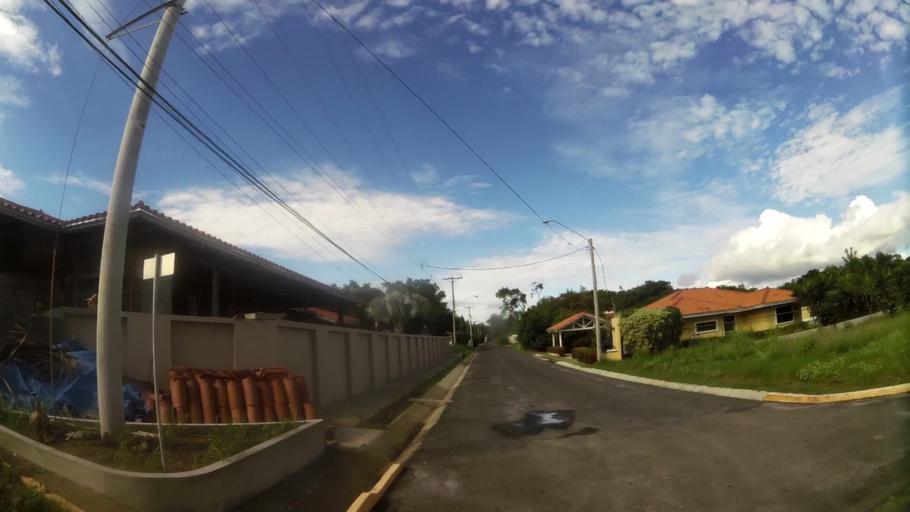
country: PA
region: Panama
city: Nueva Gorgona
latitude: 8.5411
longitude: -79.8869
